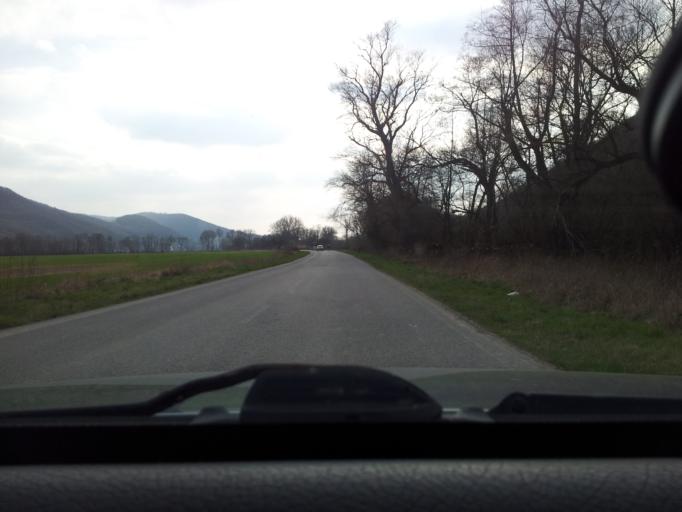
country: SK
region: Banskobystricky
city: Nova Bana
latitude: 48.4272
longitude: 18.6740
